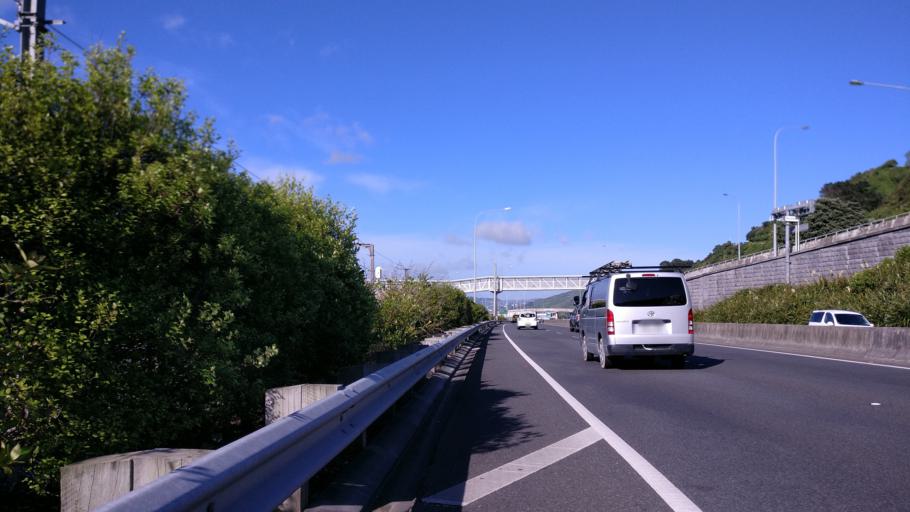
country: NZ
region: Wellington
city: Petone
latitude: -41.2208
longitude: 174.8715
